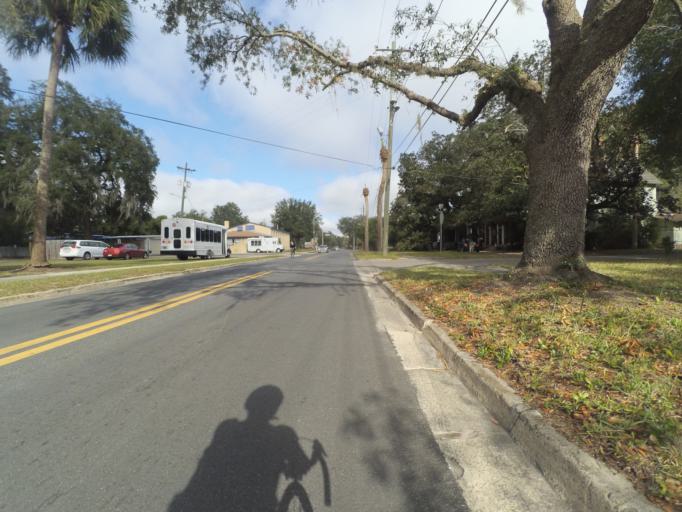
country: US
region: Florida
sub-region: Alachua County
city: Gainesville
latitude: 29.6506
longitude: -82.3177
